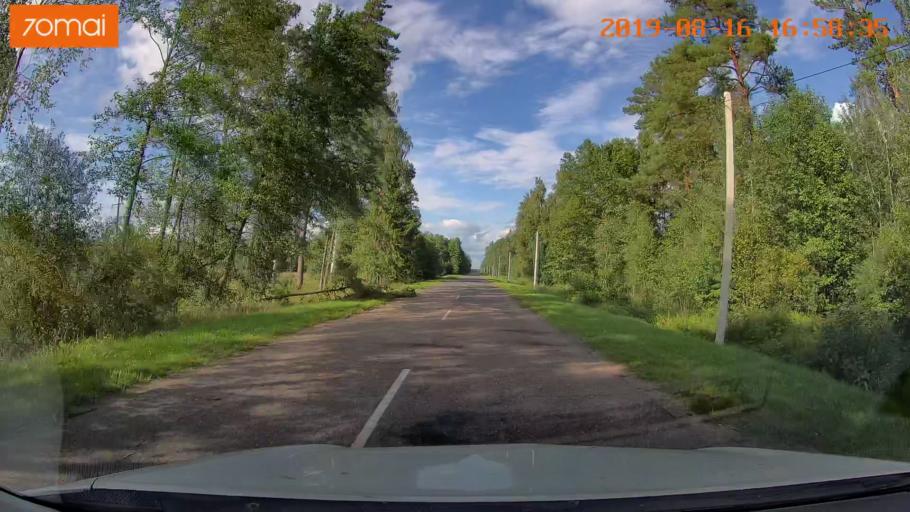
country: BY
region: Mogilev
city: Hlusha
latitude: 53.2713
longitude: 28.8346
